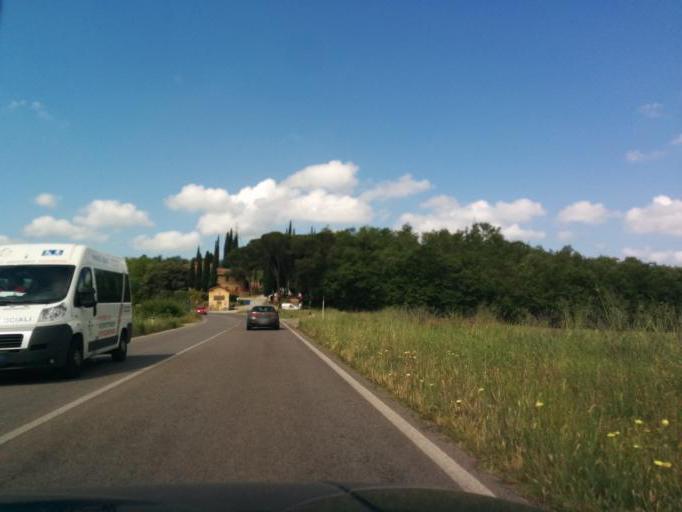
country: IT
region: Tuscany
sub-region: Provincia di Siena
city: Poggibonsi
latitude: 43.4591
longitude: 11.0947
